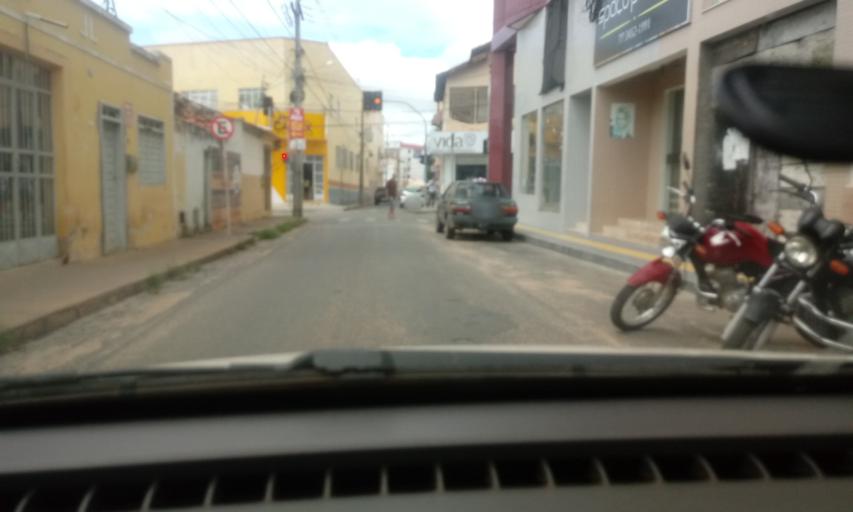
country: BR
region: Bahia
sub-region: Guanambi
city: Guanambi
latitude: -14.2237
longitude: -42.7804
